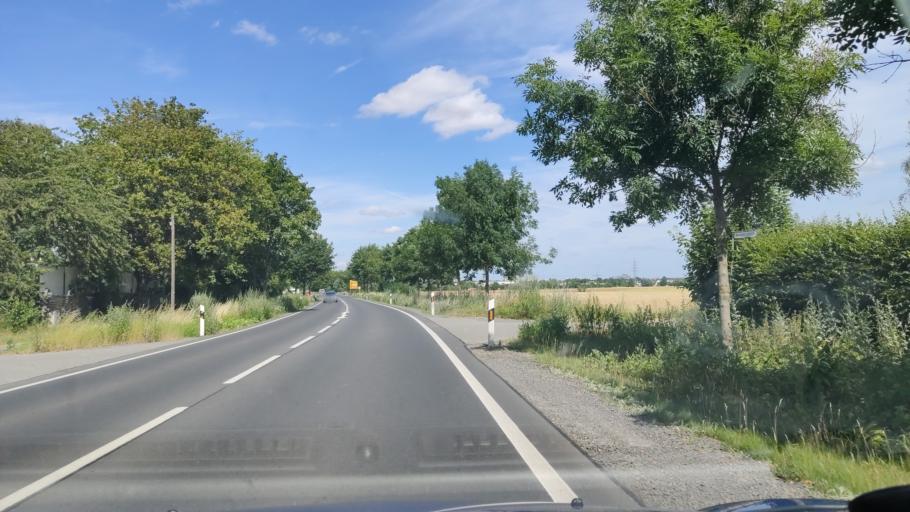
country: DE
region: Lower Saxony
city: Ronnenberg
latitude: 52.3328
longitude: 9.6396
